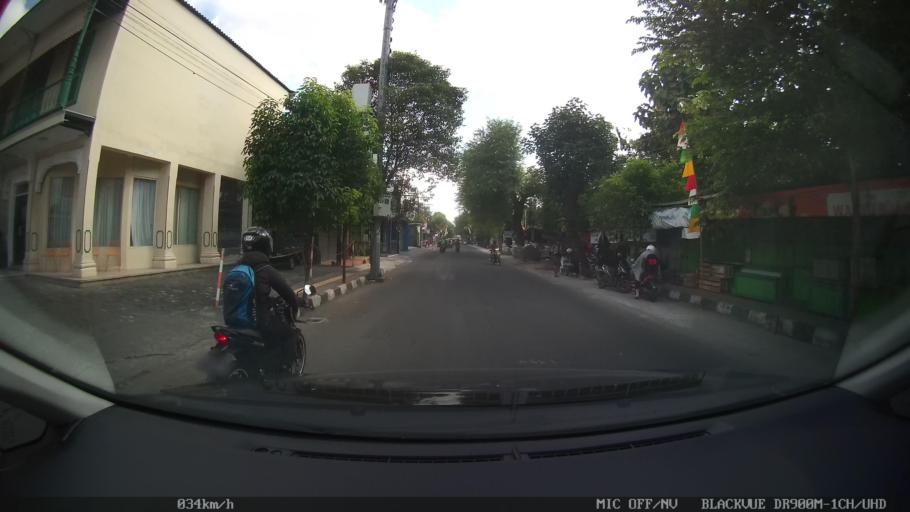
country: ID
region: Daerah Istimewa Yogyakarta
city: Yogyakarta
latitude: -7.8192
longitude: 110.3732
